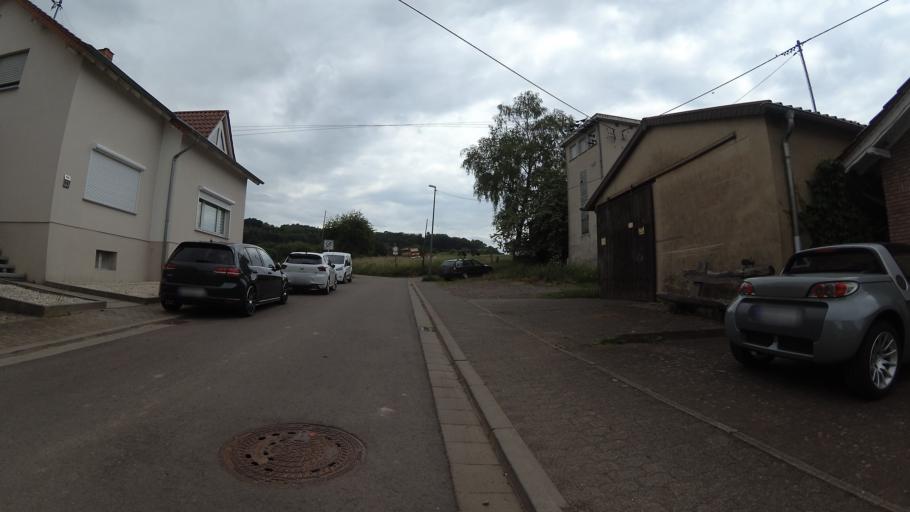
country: DE
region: Saarland
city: Tholey
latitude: 49.4944
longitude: 7.0242
